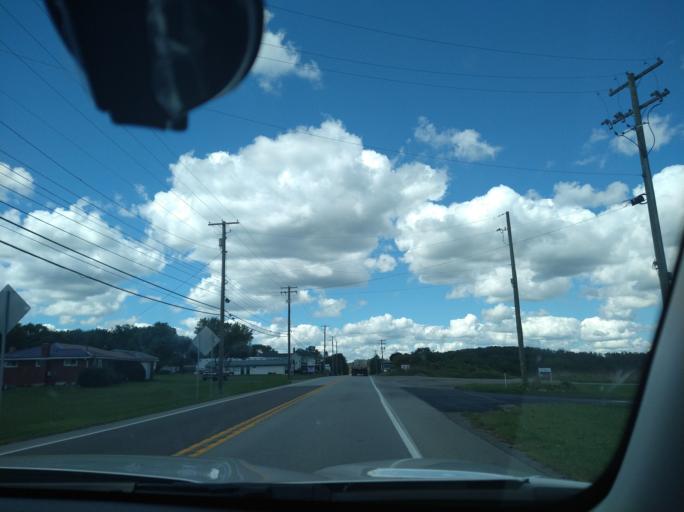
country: US
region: Pennsylvania
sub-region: Fayette County
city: Bear Rocks
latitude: 40.1042
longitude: -79.3710
